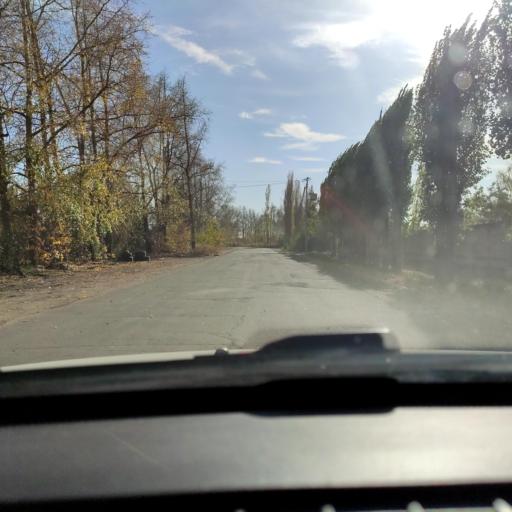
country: RU
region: Voronezj
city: Podgornoye
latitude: 51.8047
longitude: 39.1993
